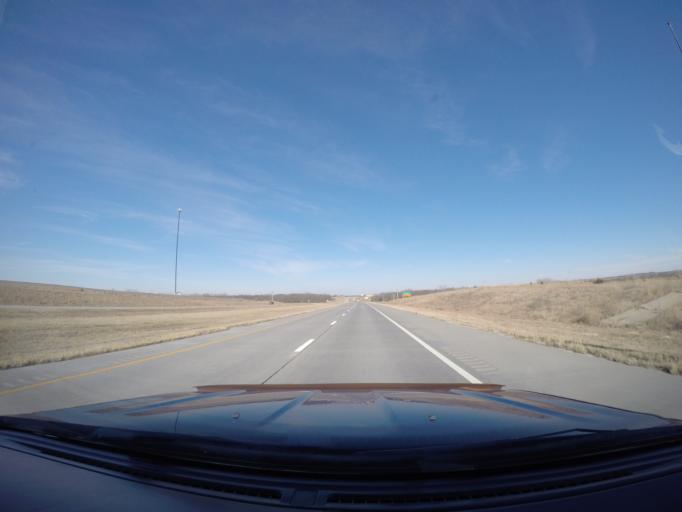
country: US
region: Kansas
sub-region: Cloud County
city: Concordia
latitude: 39.6935
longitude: -97.6600
